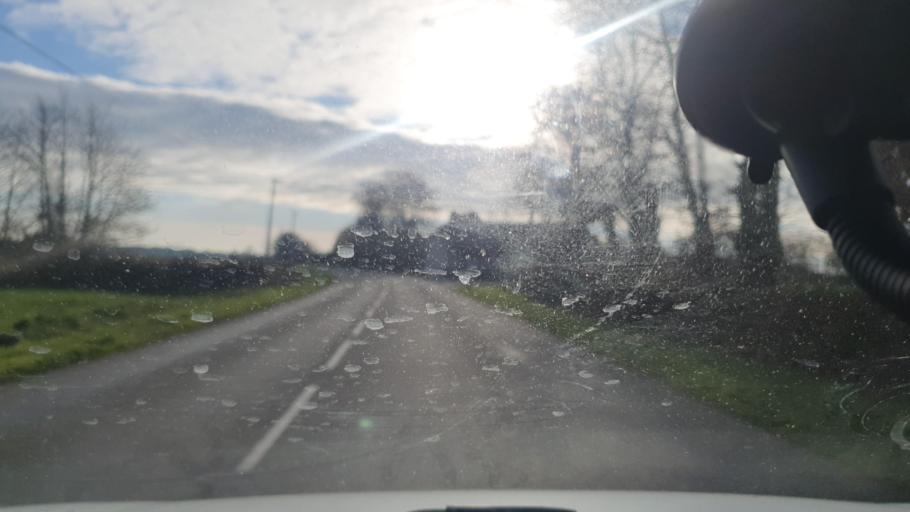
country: FR
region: Brittany
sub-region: Departement du Finistere
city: Briec
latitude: 48.0825
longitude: -4.0096
